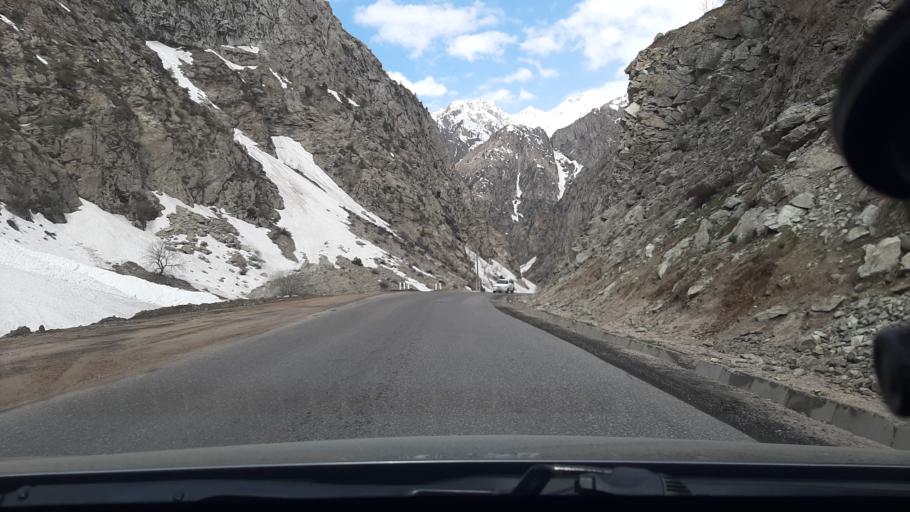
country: TJ
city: Tagob
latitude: 38.9651
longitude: 68.7685
